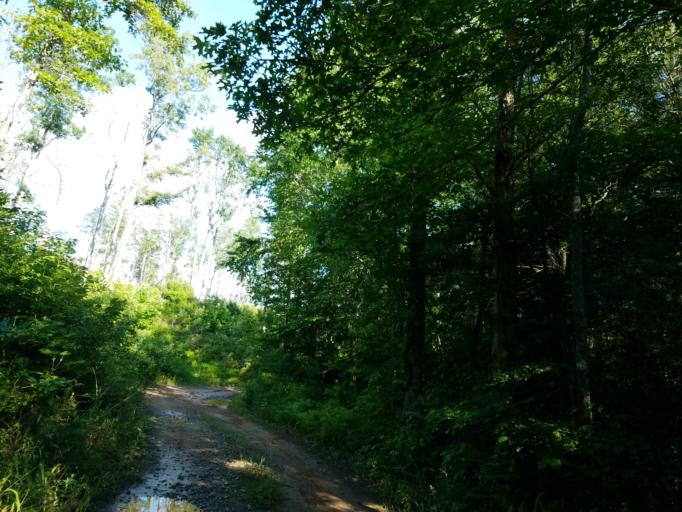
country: US
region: Georgia
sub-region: Fannin County
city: Blue Ridge
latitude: 34.7952
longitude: -84.1991
